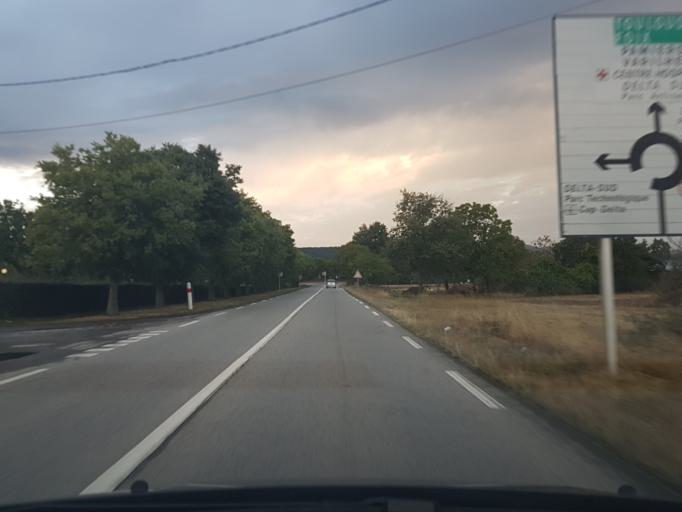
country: FR
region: Midi-Pyrenees
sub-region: Departement de l'Ariege
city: Verniolle
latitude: 43.0756
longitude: 1.6478
